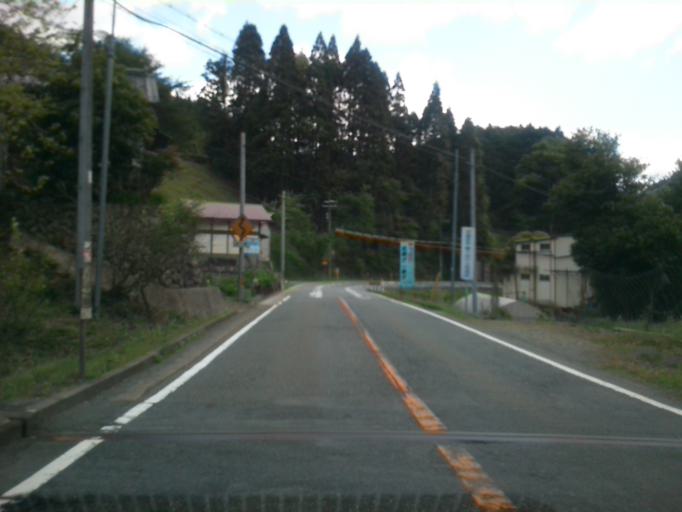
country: JP
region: Kyoto
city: Fukuchiyama
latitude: 35.3505
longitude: 135.0620
